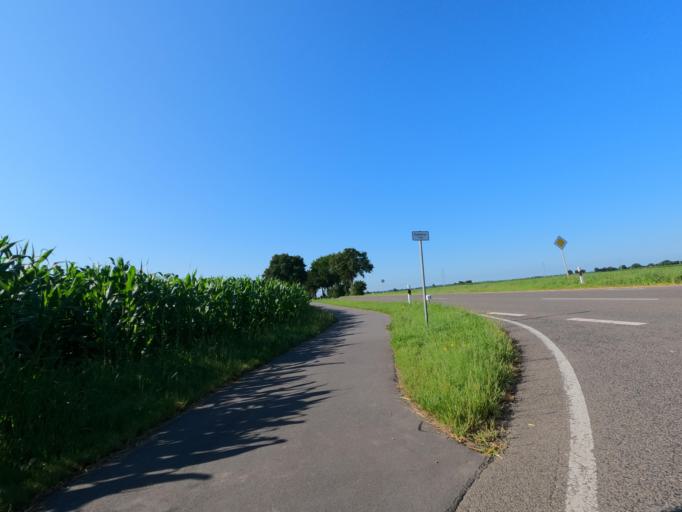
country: DE
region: North Rhine-Westphalia
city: Erkelenz
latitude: 51.0893
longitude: 6.3641
